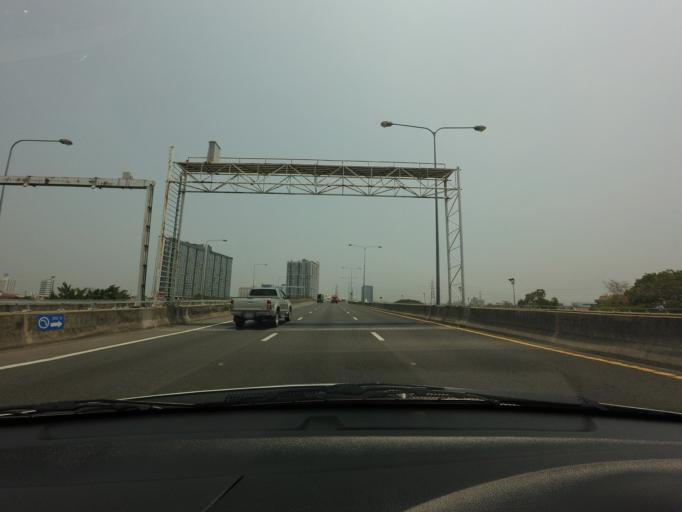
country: TH
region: Bangkok
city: Watthana
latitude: 13.7357
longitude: 100.6041
